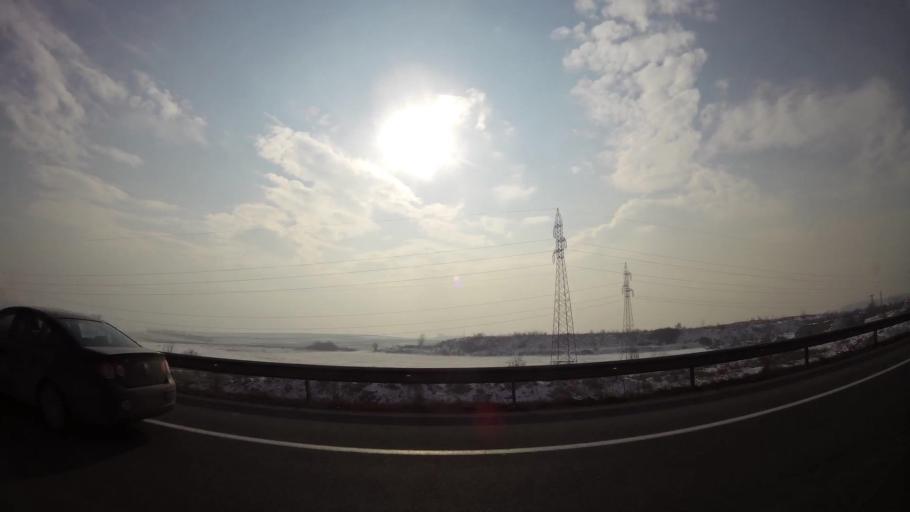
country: MK
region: Butel
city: Butel
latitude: 42.0334
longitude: 21.4742
